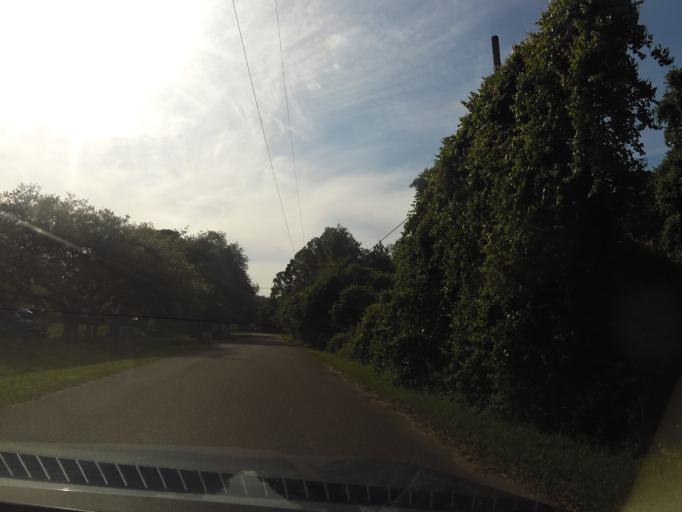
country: US
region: Florida
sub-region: Nassau County
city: Fernandina Beach
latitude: 30.5253
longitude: -81.4901
